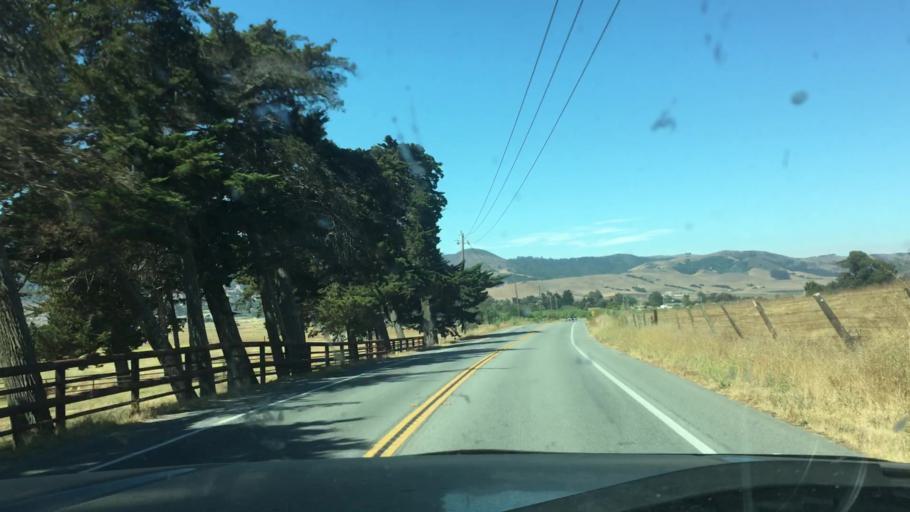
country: US
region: California
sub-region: San Luis Obispo County
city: San Luis Obispo
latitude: 35.2881
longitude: -120.6960
